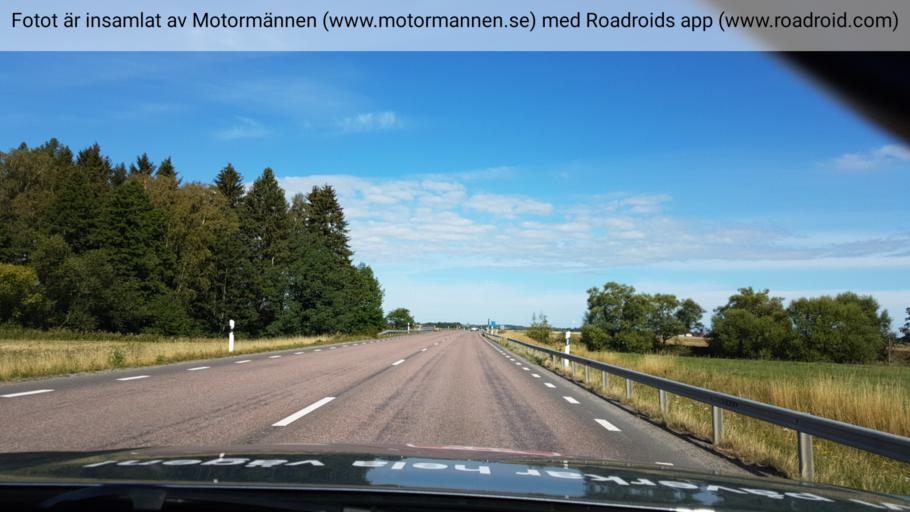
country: SE
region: Uppsala
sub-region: Uppsala Kommun
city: Gamla Uppsala
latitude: 59.8962
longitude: 17.5498
